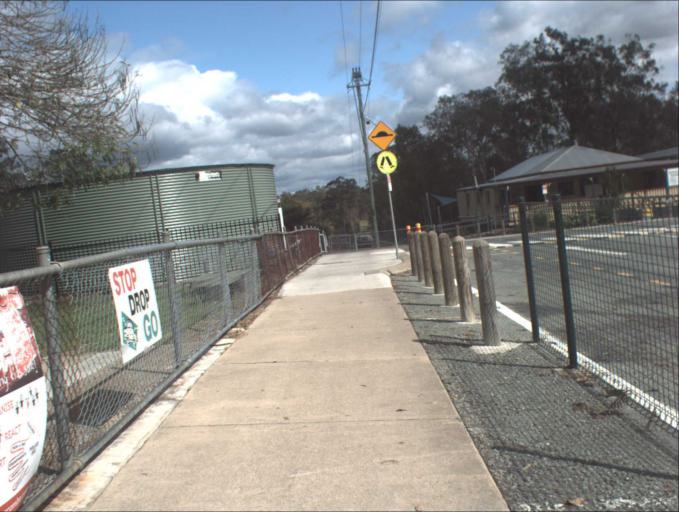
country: AU
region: Queensland
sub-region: Logan
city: Park Ridge South
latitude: -27.7099
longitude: 152.9772
